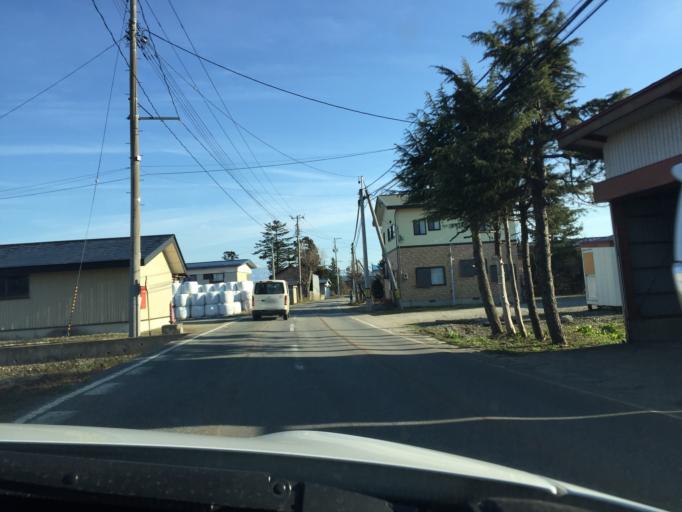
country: JP
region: Yamagata
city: Nagai
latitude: 38.0001
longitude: 140.0561
